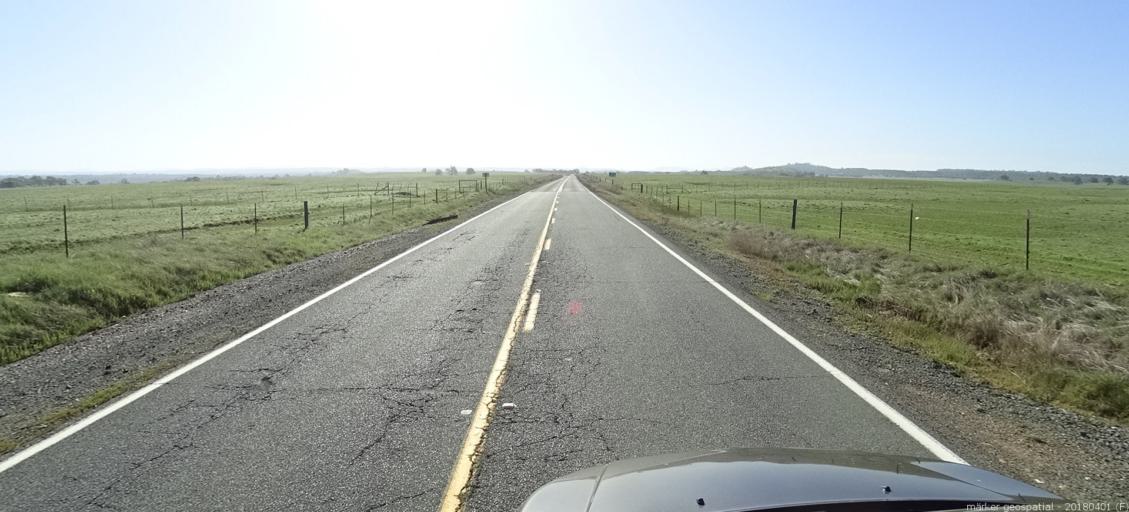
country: US
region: California
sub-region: Amador County
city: Ione
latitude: 38.4084
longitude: -121.0282
